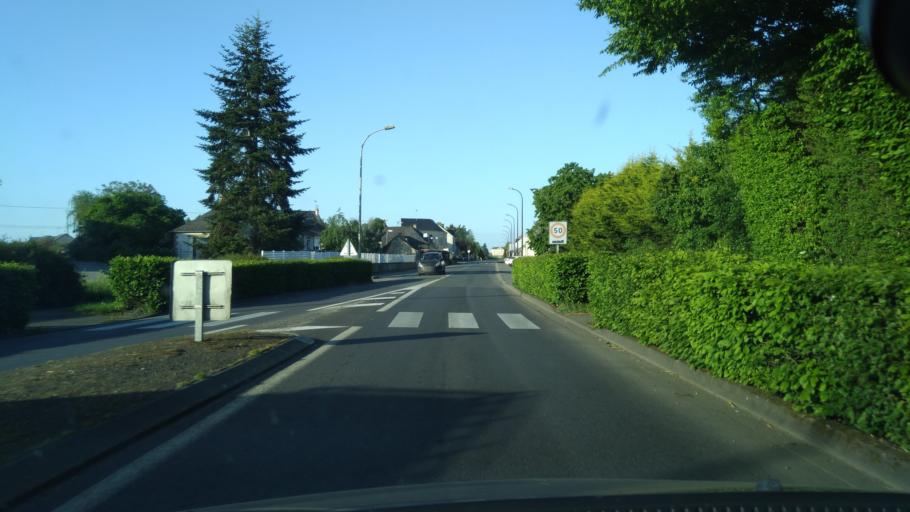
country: FR
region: Pays de la Loire
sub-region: Departement de la Mayenne
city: Craon
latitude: 47.8455
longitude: -0.9639
